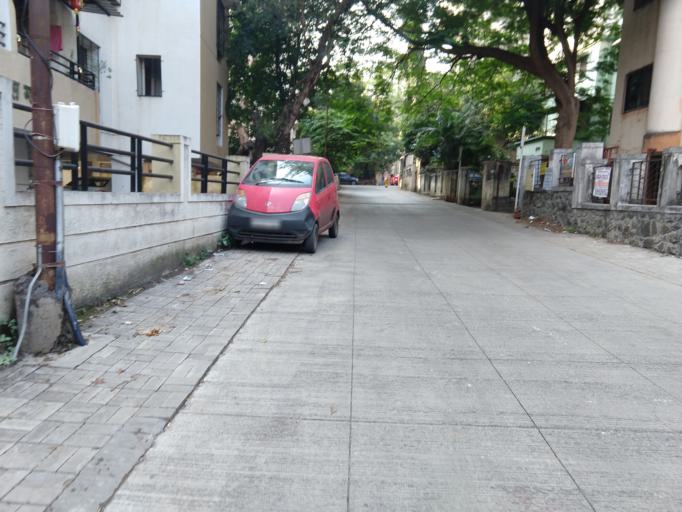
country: IN
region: Maharashtra
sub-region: Pune Division
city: Shivaji Nagar
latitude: 18.5094
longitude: 73.7910
